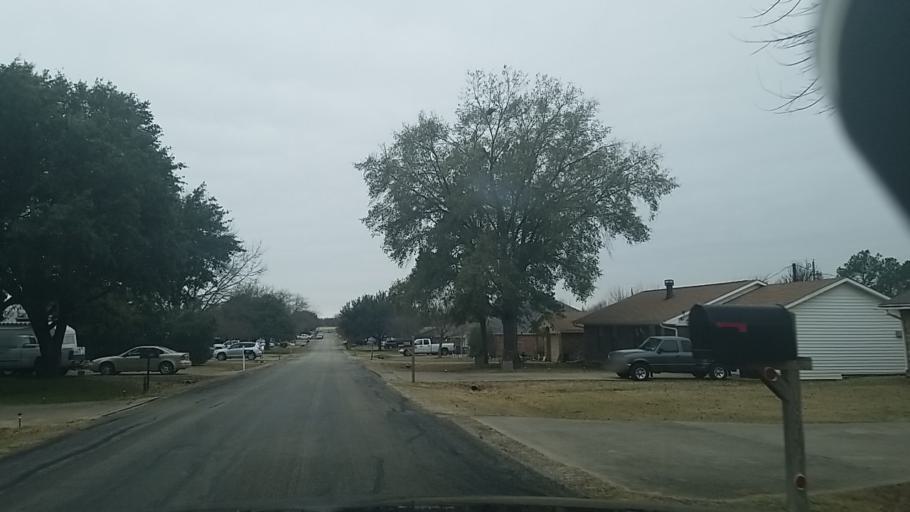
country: US
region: Texas
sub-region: Denton County
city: Corinth
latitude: 33.1511
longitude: -97.0665
